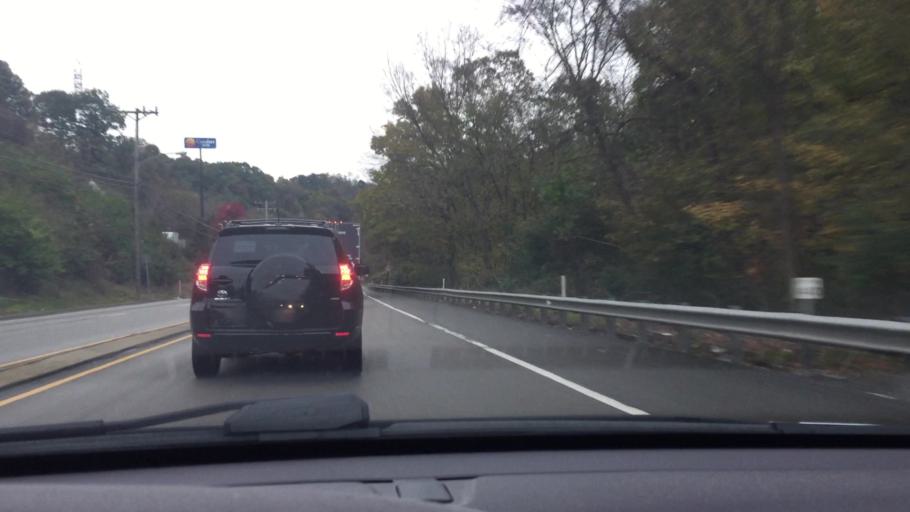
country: US
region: Pennsylvania
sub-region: Allegheny County
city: Ingram
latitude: 40.4487
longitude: -80.1059
